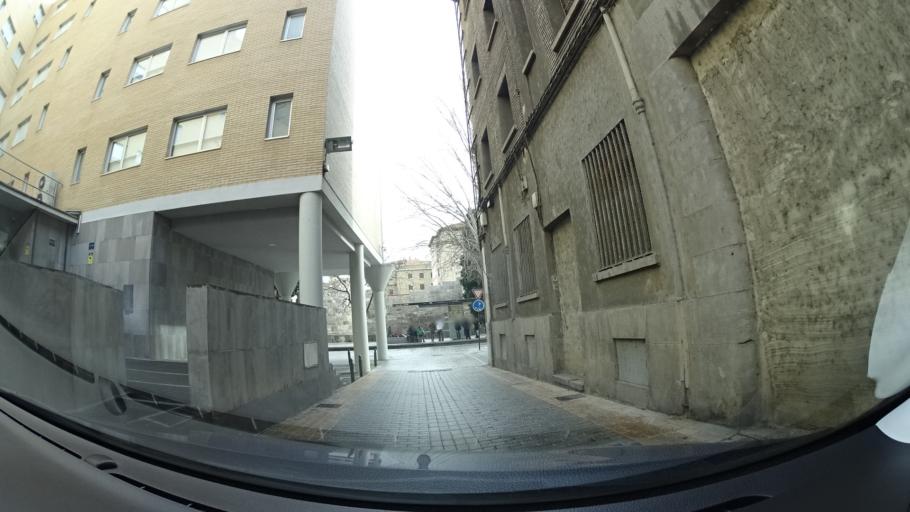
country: ES
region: Aragon
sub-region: Provincia de Zaragoza
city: Zaragoza
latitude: 41.6578
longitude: -0.8821
